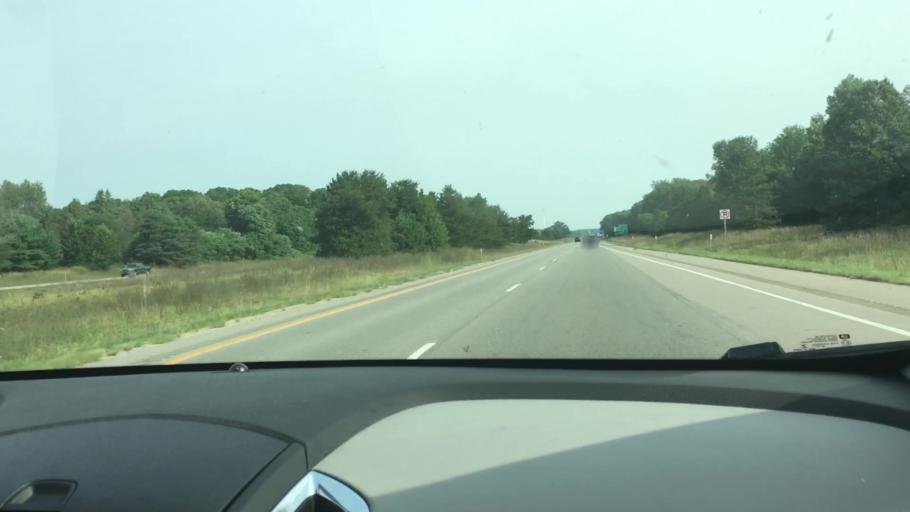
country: US
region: Michigan
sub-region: Kalamazoo County
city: Schoolcraft
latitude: 42.1765
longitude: -85.6452
